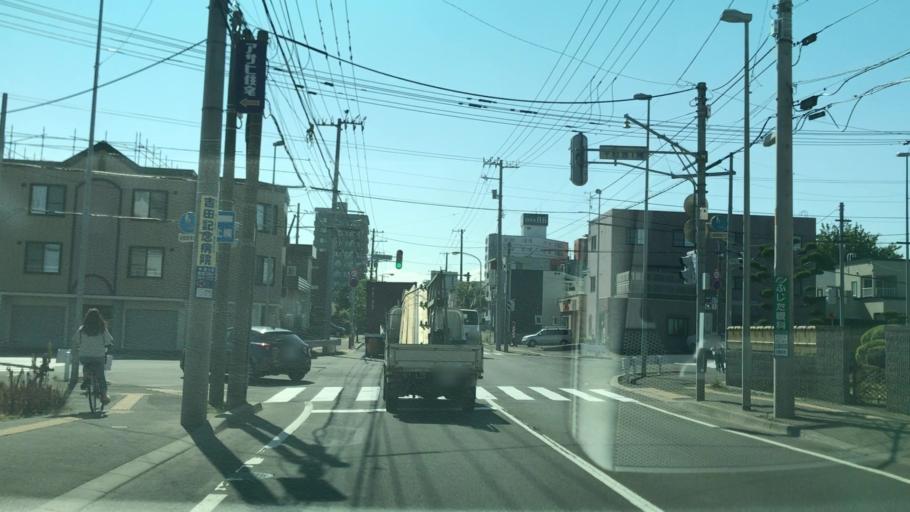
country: JP
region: Hokkaido
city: Sapporo
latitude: 43.0544
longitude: 141.4076
